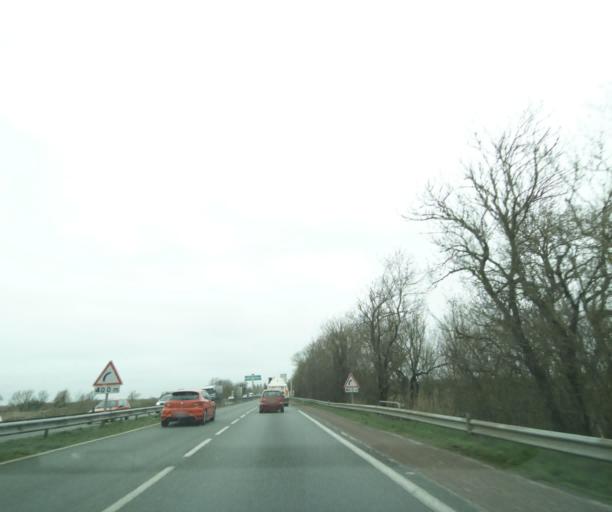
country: FR
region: Poitou-Charentes
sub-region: Departement de la Charente-Maritime
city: Angoulins
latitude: 46.1171
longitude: -1.1063
